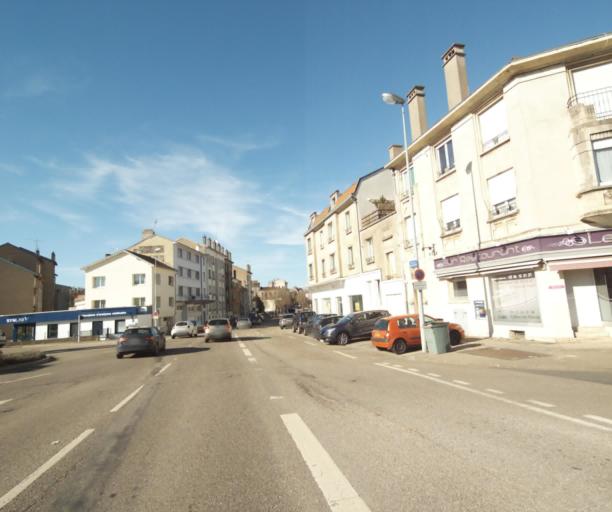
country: FR
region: Lorraine
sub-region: Departement de Meurthe-et-Moselle
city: Nancy
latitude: 48.6738
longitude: 6.1835
